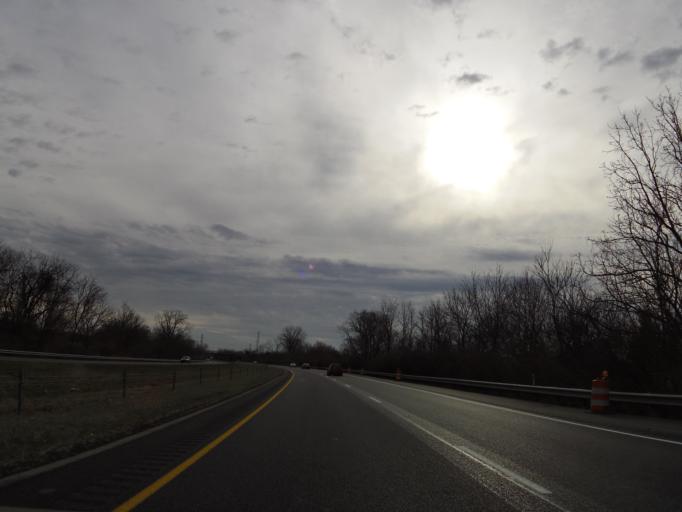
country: US
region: Indiana
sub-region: Marion County
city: Clermont
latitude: 39.8194
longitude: -86.3044
